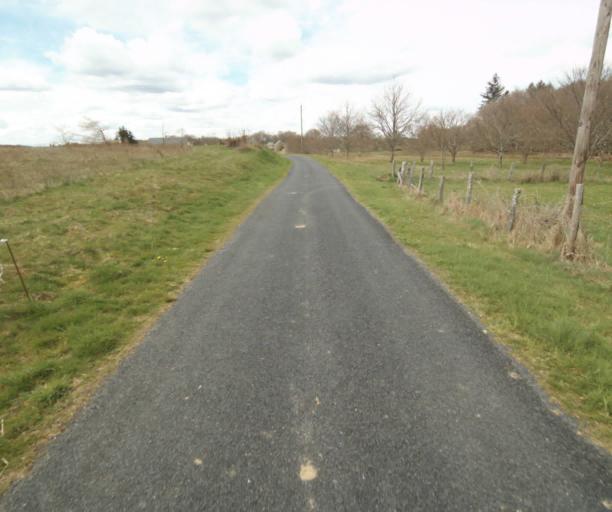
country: FR
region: Limousin
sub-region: Departement de la Correze
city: Argentat
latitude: 45.2177
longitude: 1.9239
